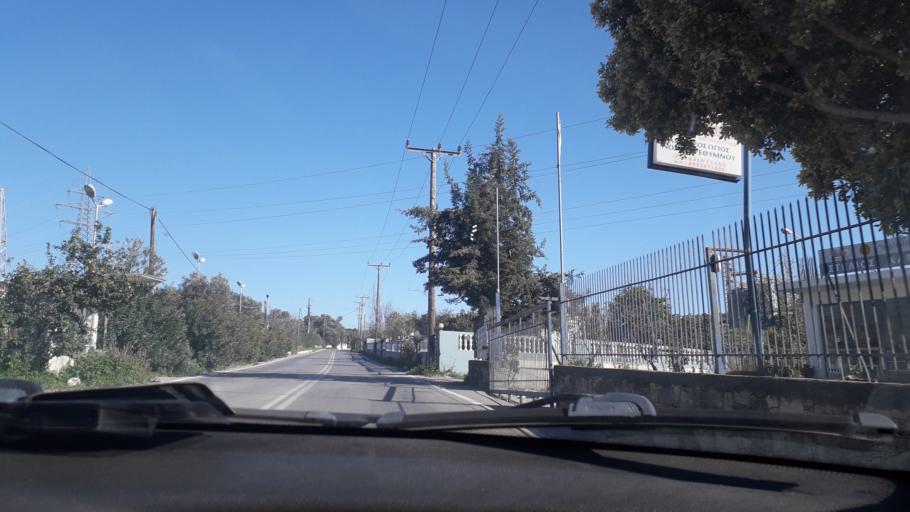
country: GR
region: Crete
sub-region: Nomos Rethymnis
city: Rethymno
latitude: 35.3607
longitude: 24.5469
